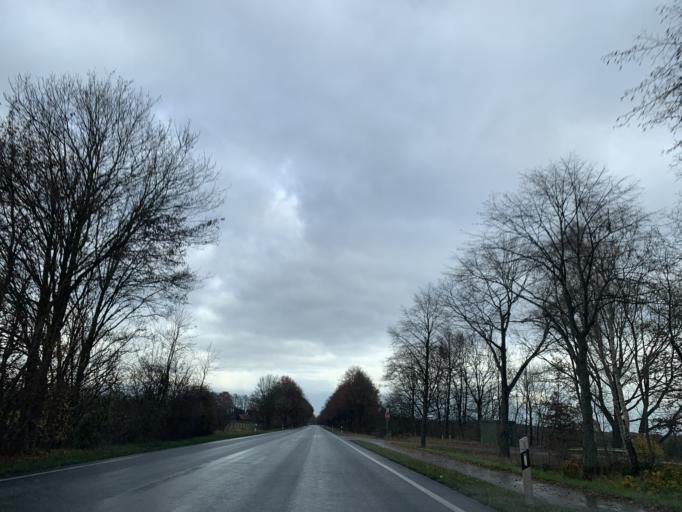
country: DE
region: North Rhine-Westphalia
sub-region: Regierungsbezirk Munster
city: Gronau
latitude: 52.1720
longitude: 6.9610
